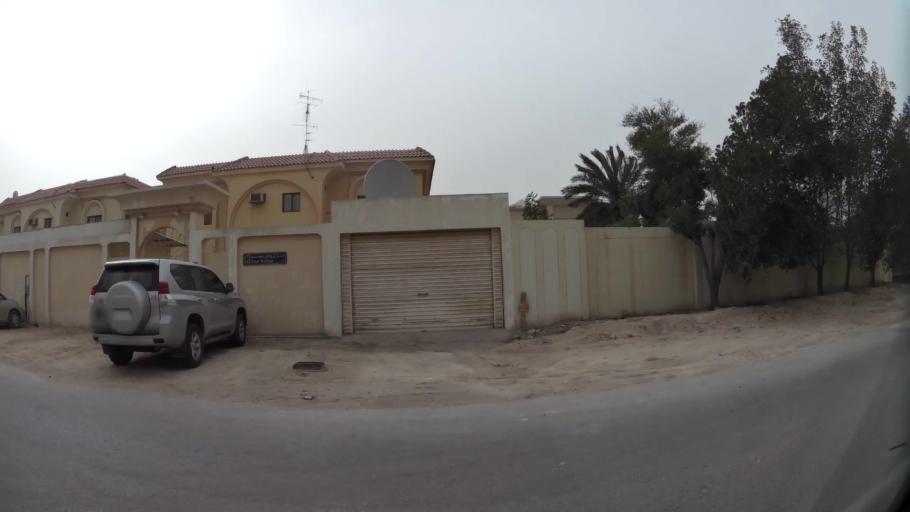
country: QA
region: Baladiyat ad Dawhah
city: Doha
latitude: 25.2517
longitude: 51.4966
